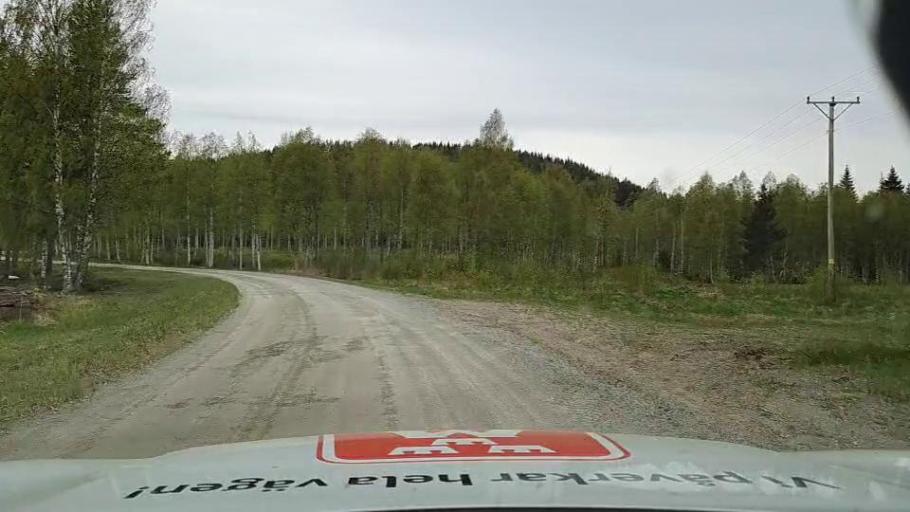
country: SE
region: Jaemtland
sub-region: Bergs Kommun
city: Hoverberg
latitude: 62.6895
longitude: 14.7791
